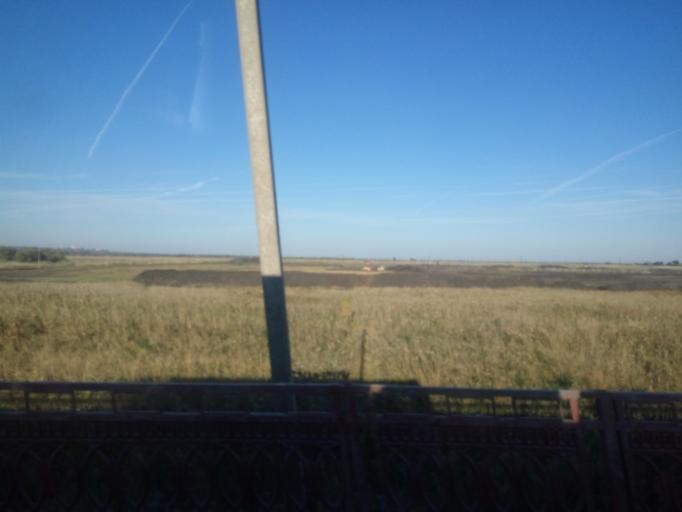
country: RU
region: Rostov
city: Bataysk
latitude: 47.1771
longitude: 39.7416
